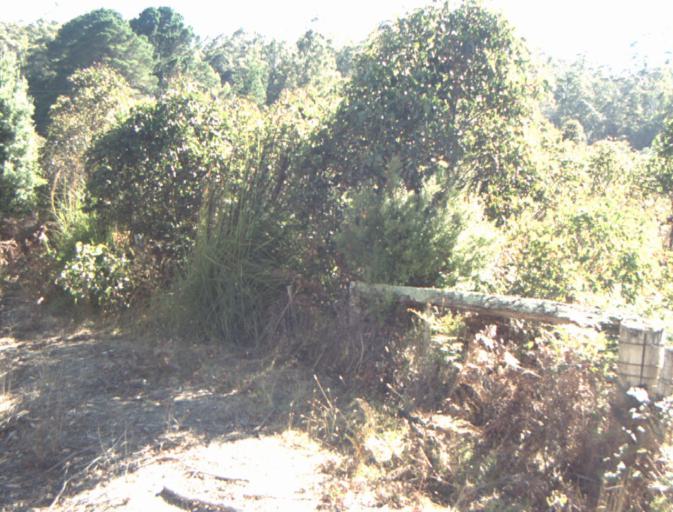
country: AU
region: Tasmania
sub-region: Dorset
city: Scottsdale
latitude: -41.2982
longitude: 147.3547
